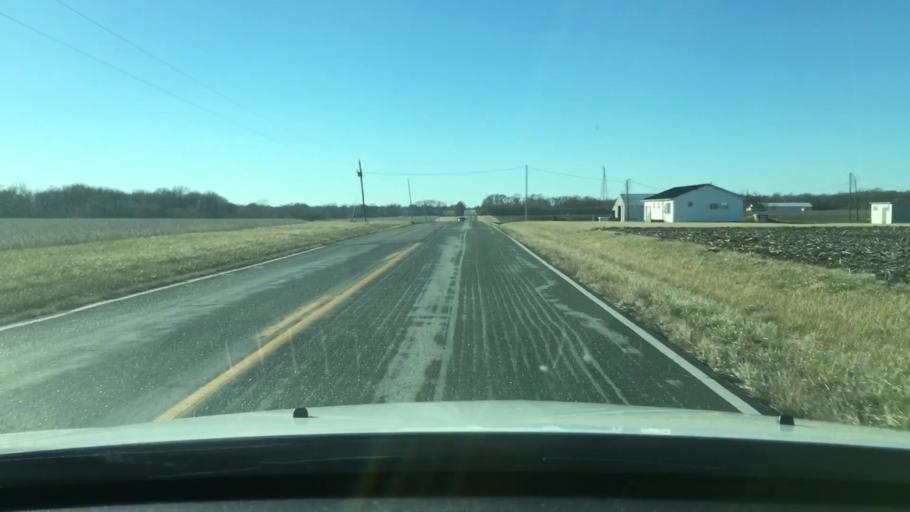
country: US
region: Missouri
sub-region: Audrain County
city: Vandalia
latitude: 39.2812
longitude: -91.6552
